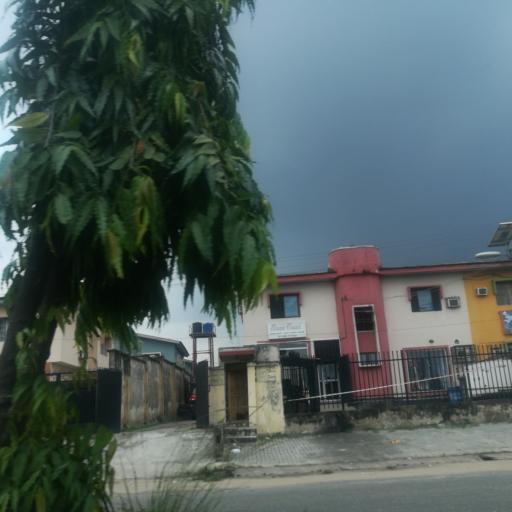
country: NG
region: Lagos
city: Ojota
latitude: 6.5801
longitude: 3.3863
